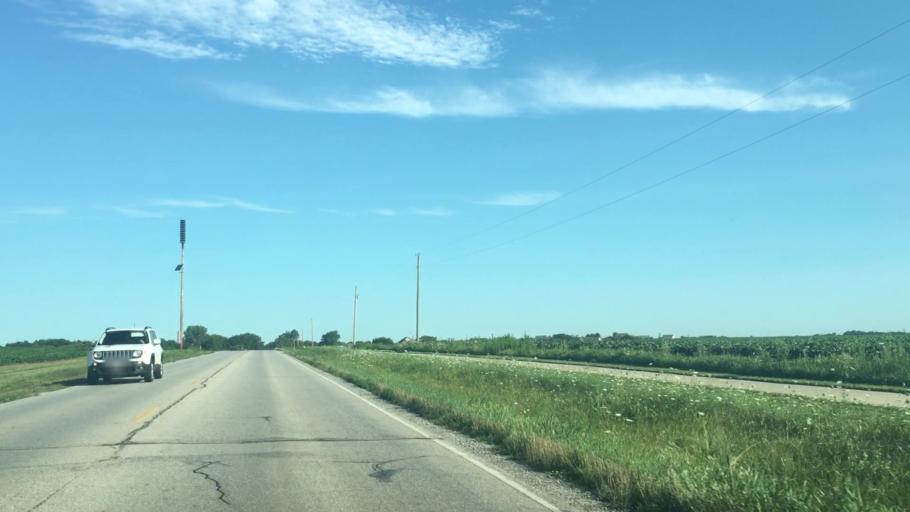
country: US
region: Iowa
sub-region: Johnson County
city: North Liberty
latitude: 41.7371
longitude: -91.5836
